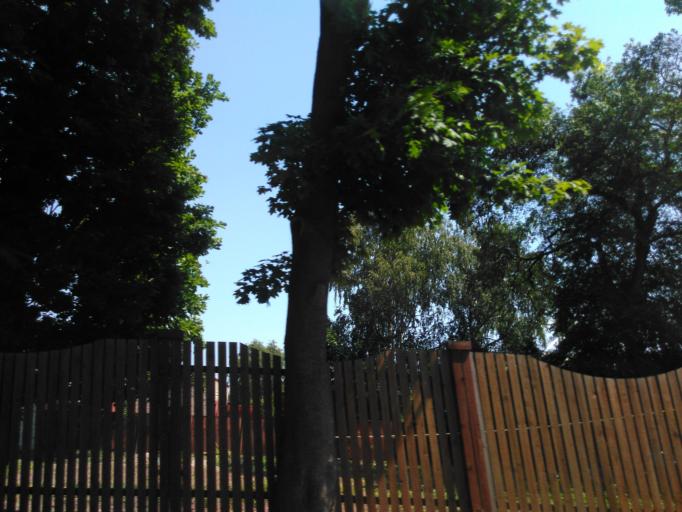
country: RU
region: Moskovskaya
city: Staraya Kupavna
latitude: 55.8085
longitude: 38.1646
